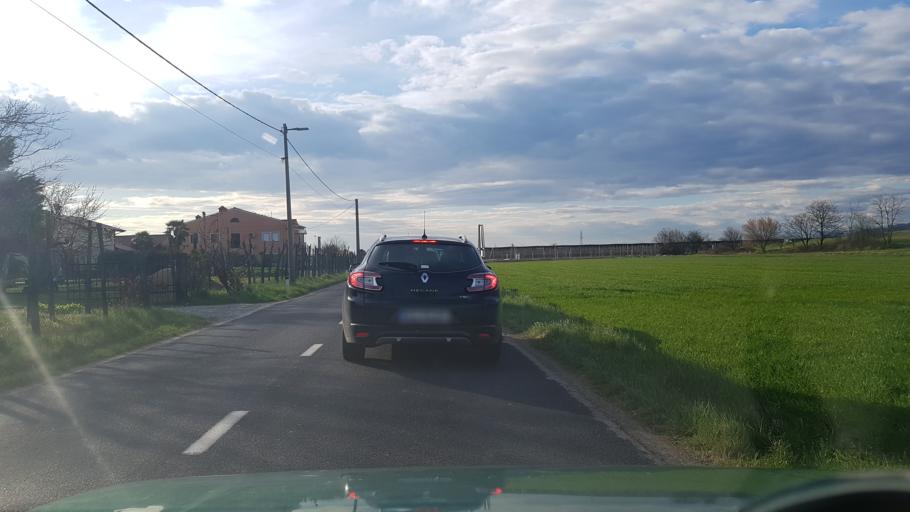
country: SI
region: Miren-Kostanjevica
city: Bilje
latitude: 45.8961
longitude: 13.6264
